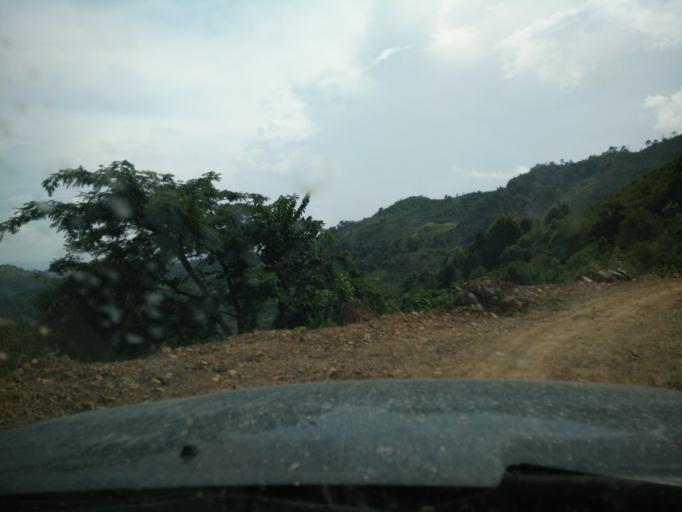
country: CN
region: Guangxi Zhuangzu Zizhiqu
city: Leli
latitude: 24.7719
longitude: 105.9083
